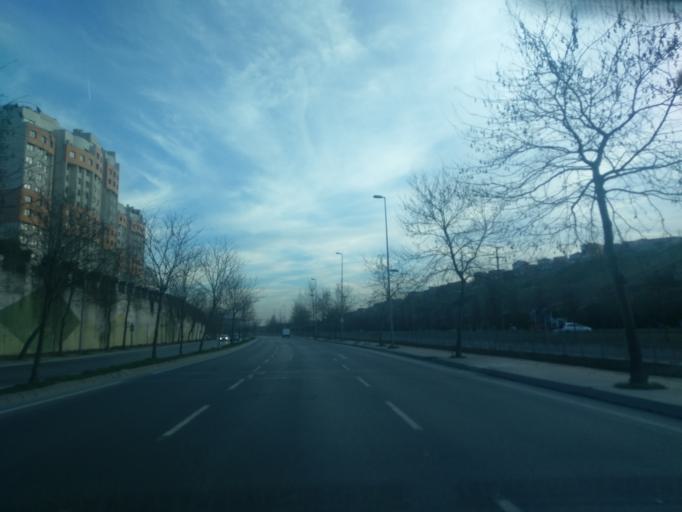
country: TR
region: Istanbul
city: Basaksehir
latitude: 41.0505
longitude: 28.7576
